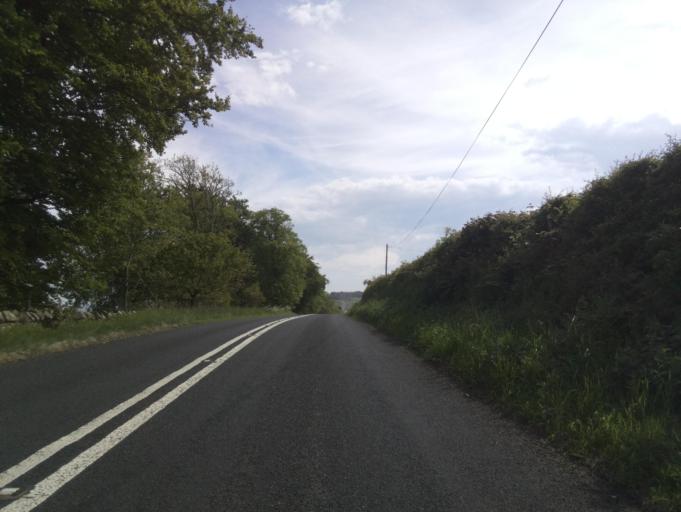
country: GB
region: England
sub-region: Northumberland
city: Alnwick
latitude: 55.4522
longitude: -1.7111
